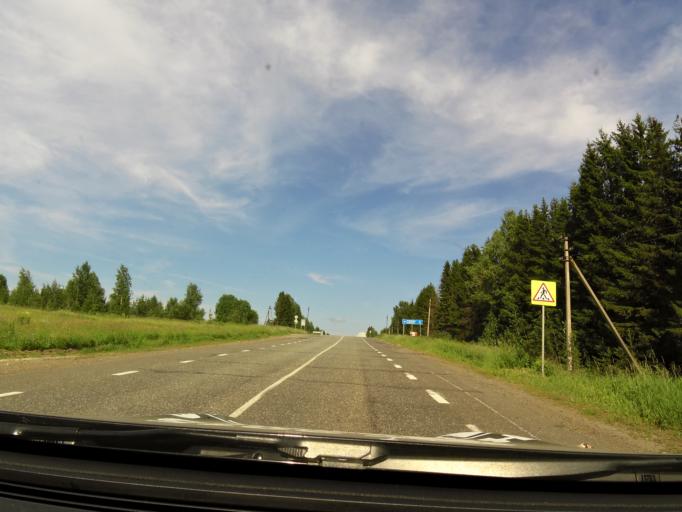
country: RU
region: Kirov
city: Belaya Kholunitsa
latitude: 58.8436
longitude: 50.7017
